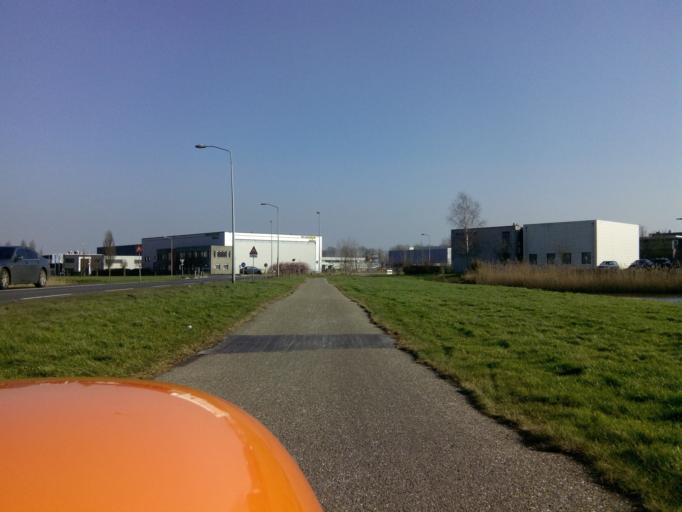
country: NL
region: Flevoland
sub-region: Gemeente Zeewolde
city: Zeewolde
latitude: 52.3533
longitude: 5.5024
